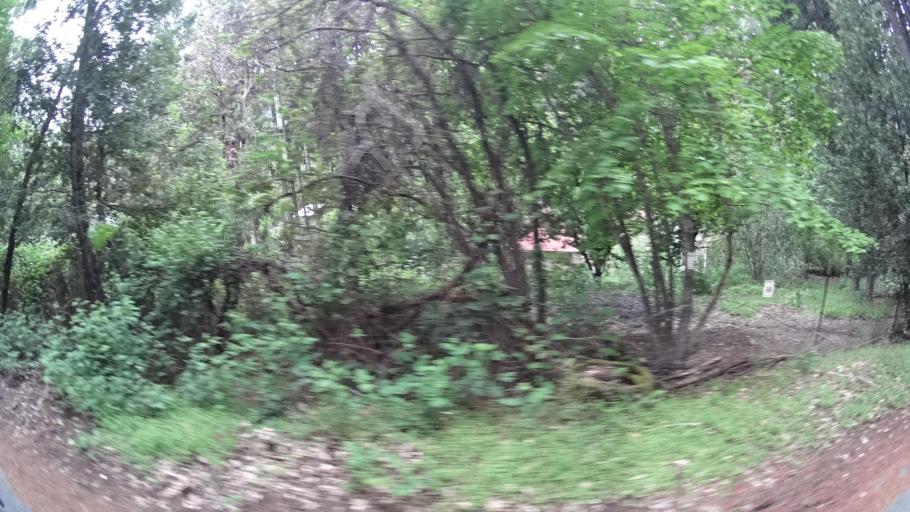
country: US
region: California
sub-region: Humboldt County
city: Willow Creek
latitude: 40.9298
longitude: -123.6160
